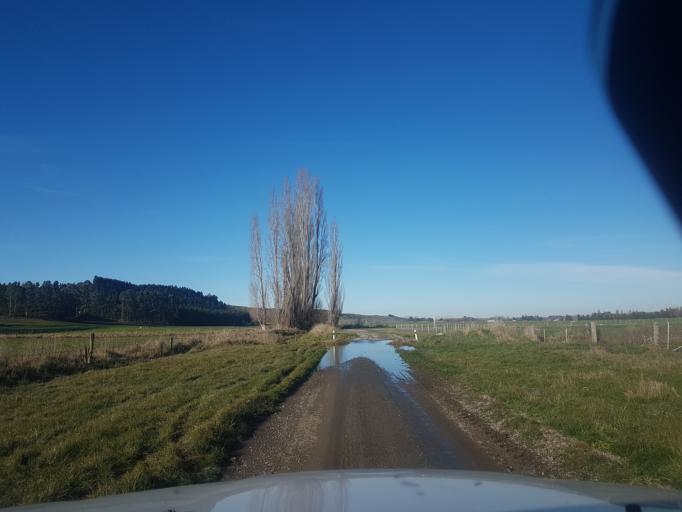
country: NZ
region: Canterbury
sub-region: Timaru District
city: Pleasant Point
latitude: -44.2222
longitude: 171.0512
